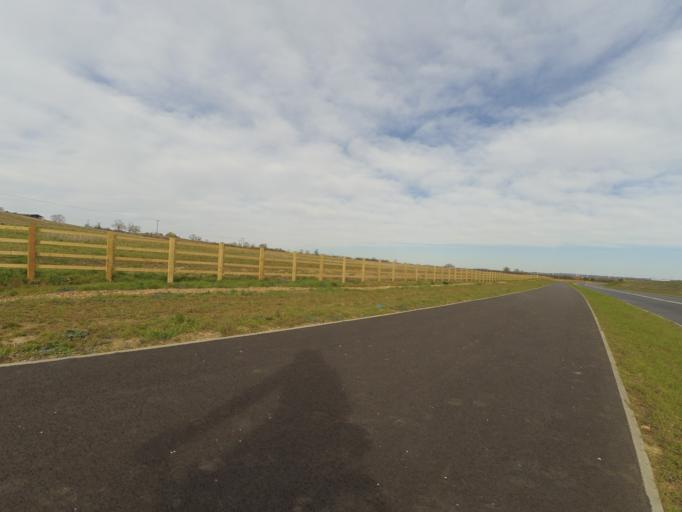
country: GB
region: England
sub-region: Warwickshire
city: Rugby
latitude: 52.3695
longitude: -1.2173
